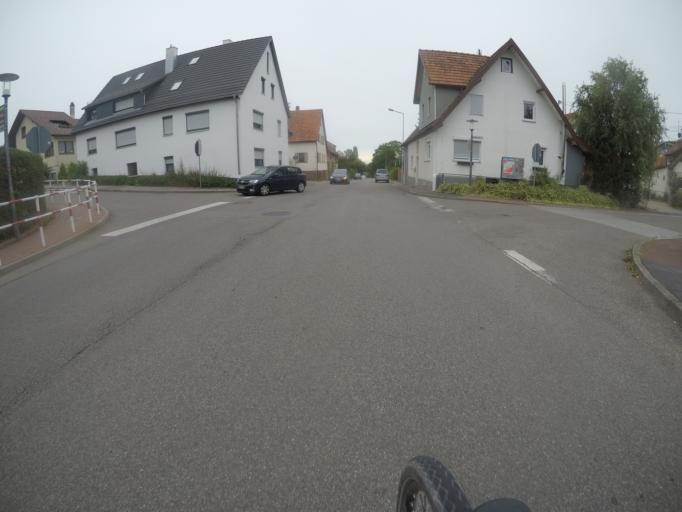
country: DE
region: Baden-Wuerttemberg
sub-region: Karlsruhe Region
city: Simmozheim
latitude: 48.7748
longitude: 8.8180
